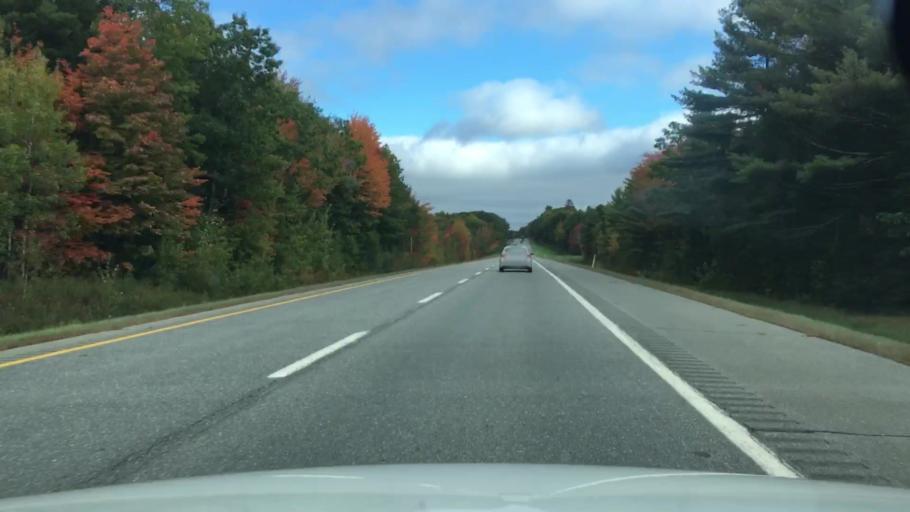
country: US
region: Maine
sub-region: Penobscot County
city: Carmel
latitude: 44.7651
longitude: -68.9922
